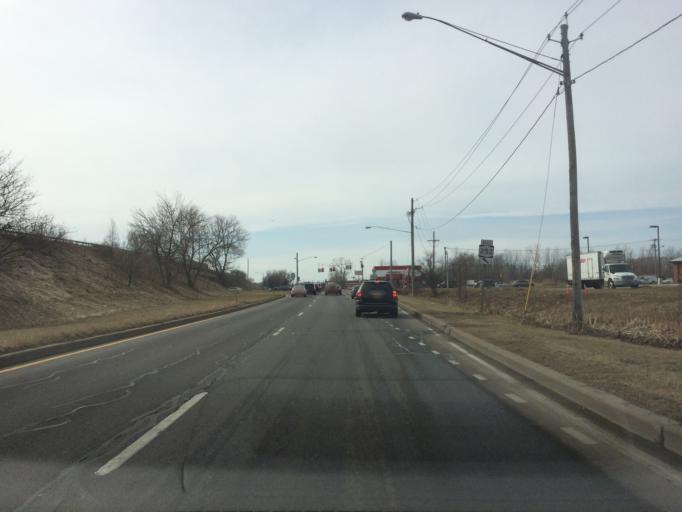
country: US
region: New York
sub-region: Monroe County
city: Rochester
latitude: 43.0880
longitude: -77.6343
